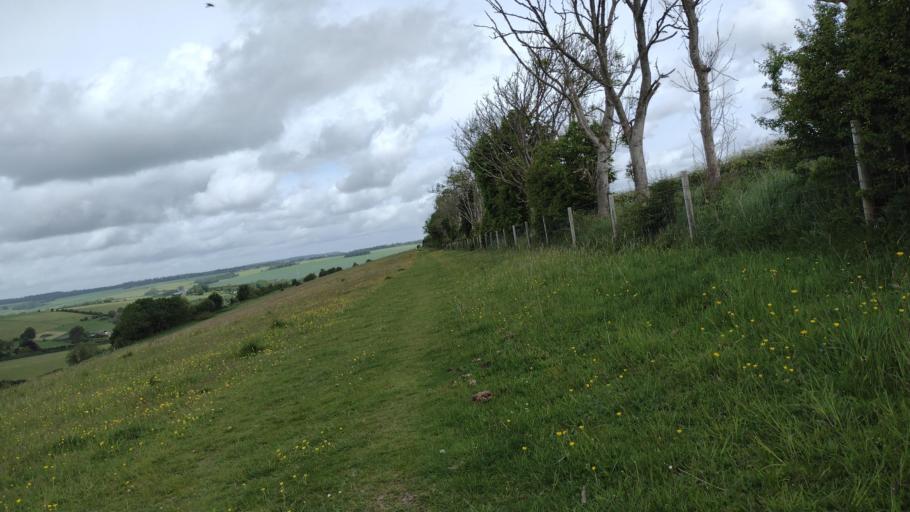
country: GB
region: England
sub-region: Wiltshire
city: Wilton
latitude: 51.0235
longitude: -1.8412
